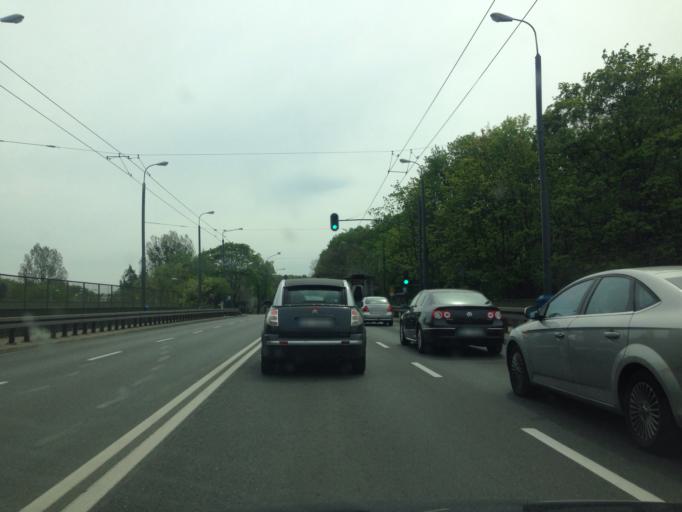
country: PL
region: Pomeranian Voivodeship
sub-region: Sopot
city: Sopot
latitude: 54.4538
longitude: 18.5556
